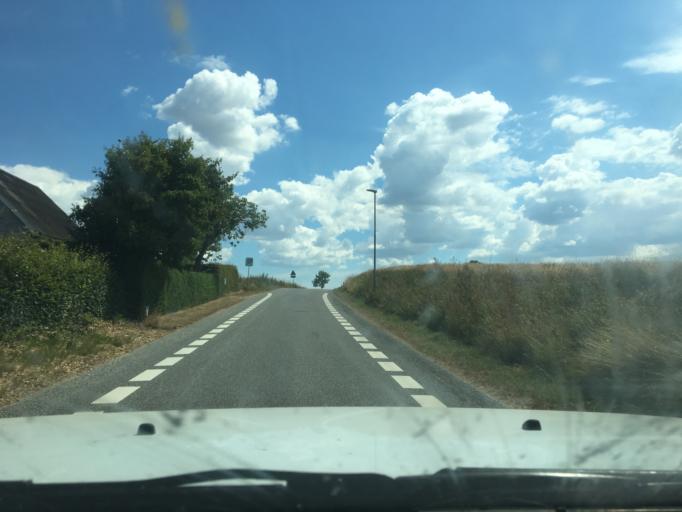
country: DK
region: Central Jutland
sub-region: Syddjurs Kommune
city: Hornslet
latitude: 56.3481
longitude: 10.2912
